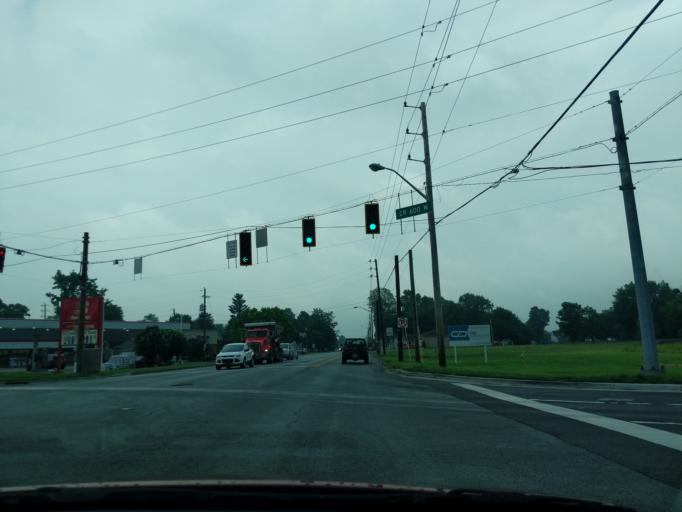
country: US
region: Indiana
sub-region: Hancock County
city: McCordsville
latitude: 39.8960
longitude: -85.9190
